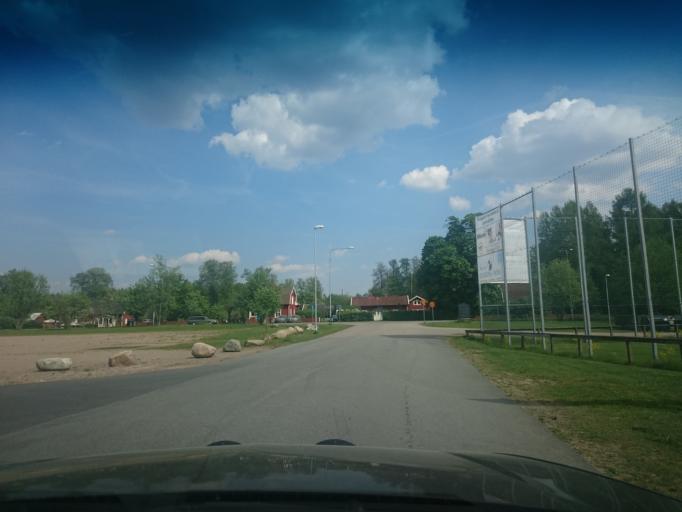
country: SE
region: Joenkoeping
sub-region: Vetlanda Kommun
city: Vetlanda
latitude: 57.4396
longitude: 15.0683
